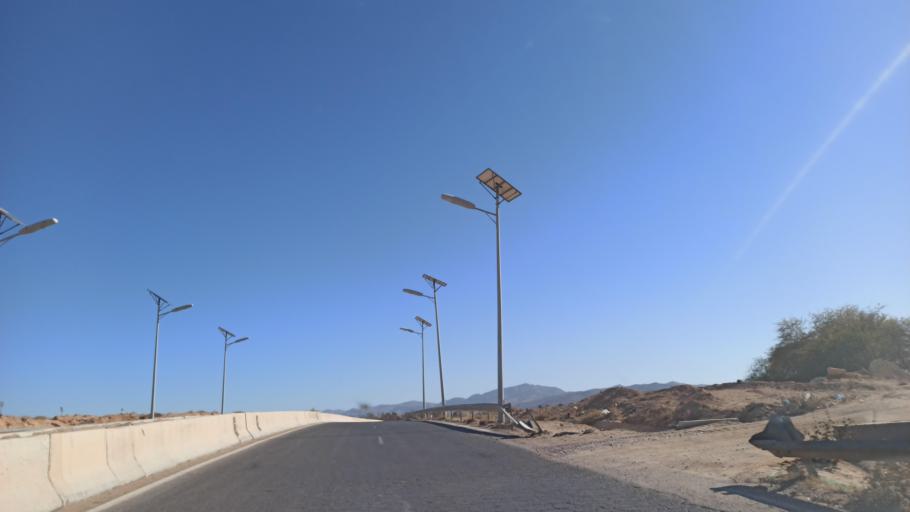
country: TN
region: Gafsa
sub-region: Gafsa Municipality
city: Gafsa
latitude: 34.4328
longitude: 8.8111
